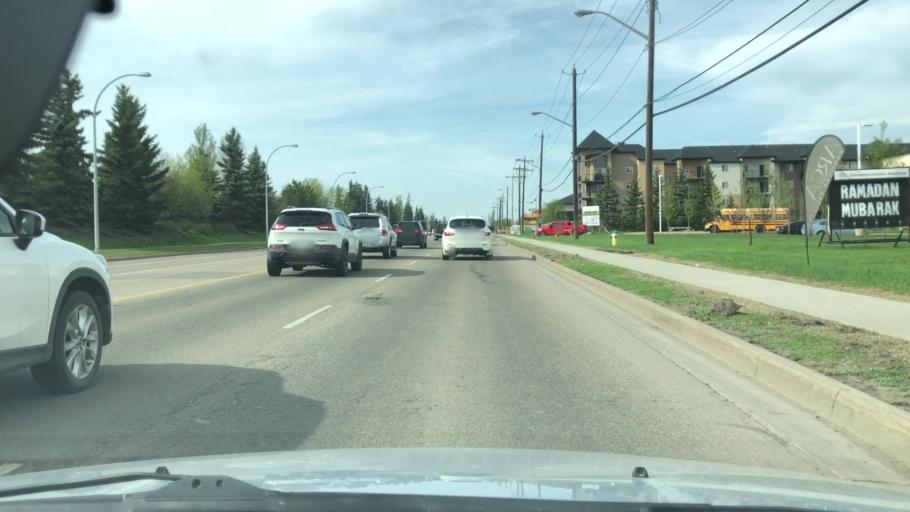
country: CA
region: Alberta
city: Edmonton
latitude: 53.6070
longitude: -113.5412
